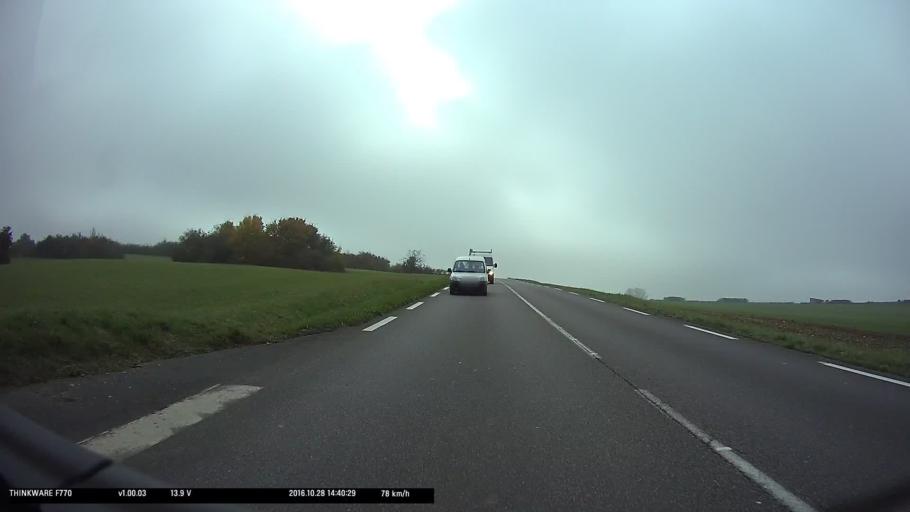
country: FR
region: Lorraine
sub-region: Departement de la Moselle
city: Lorquin
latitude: 48.6765
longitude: 6.9493
